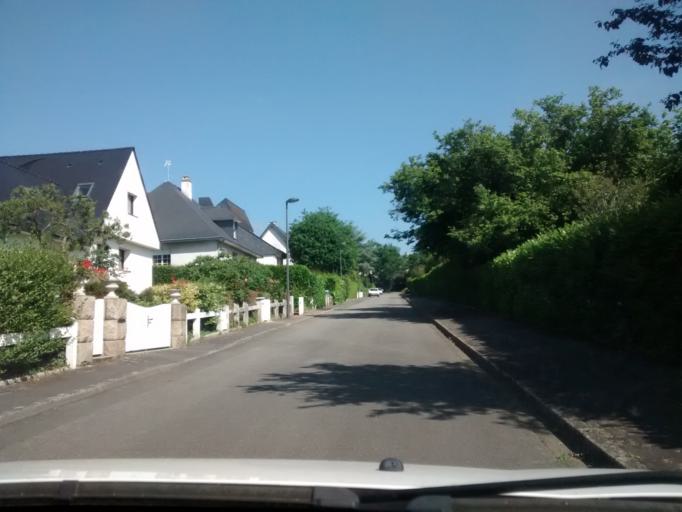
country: FR
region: Brittany
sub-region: Departement d'Ille-et-Vilaine
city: Cesson-Sevigne
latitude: 48.1204
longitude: -1.6088
